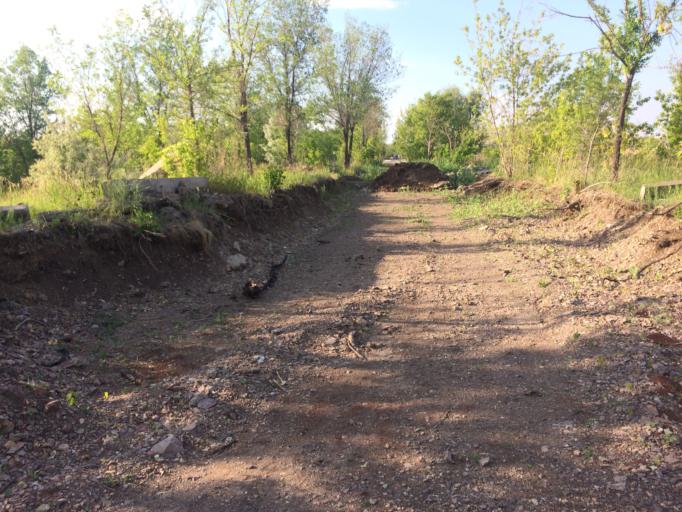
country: RU
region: Chelyabinsk
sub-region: Gorod Magnitogorsk
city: Magnitogorsk
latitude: 53.4004
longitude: 58.9946
